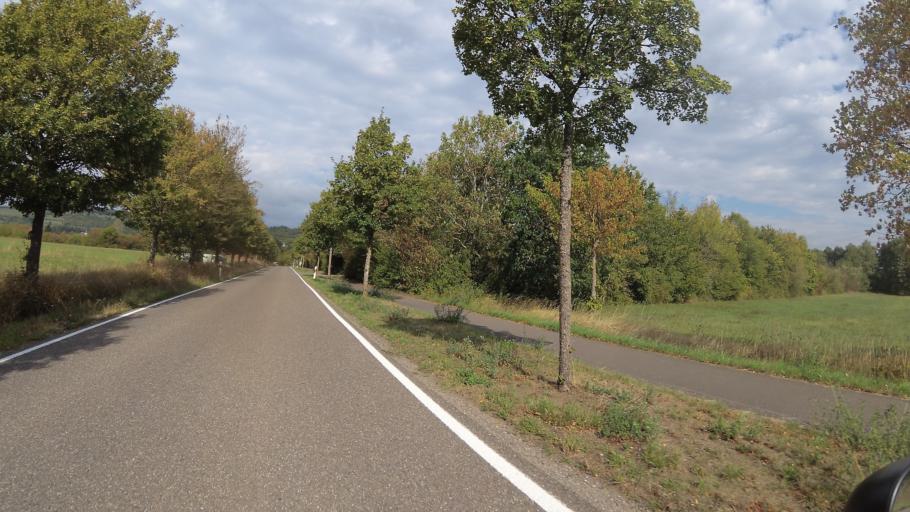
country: DE
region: Saarland
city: Gersheim
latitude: 49.1342
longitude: 7.1959
